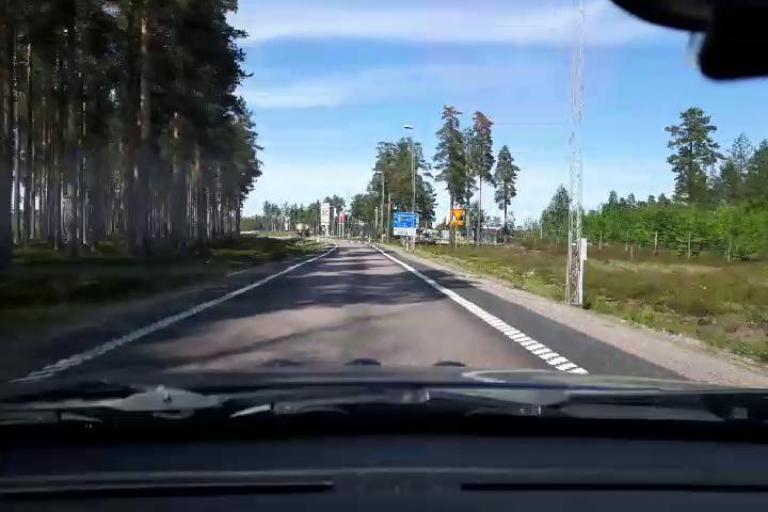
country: SE
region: Gaevleborg
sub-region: Gavle Kommun
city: Norrsundet
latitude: 61.0700
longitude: 16.9653
